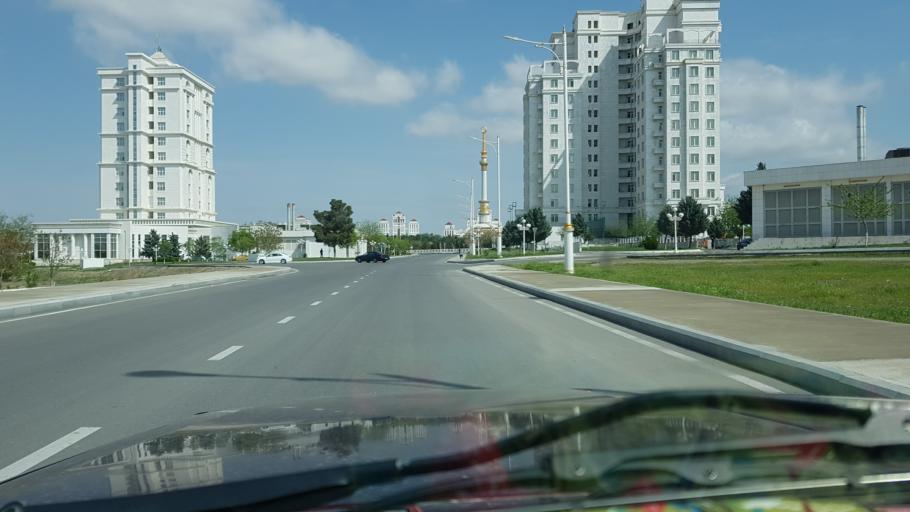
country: TM
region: Ahal
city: Ashgabat
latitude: 37.8818
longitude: 58.3739
